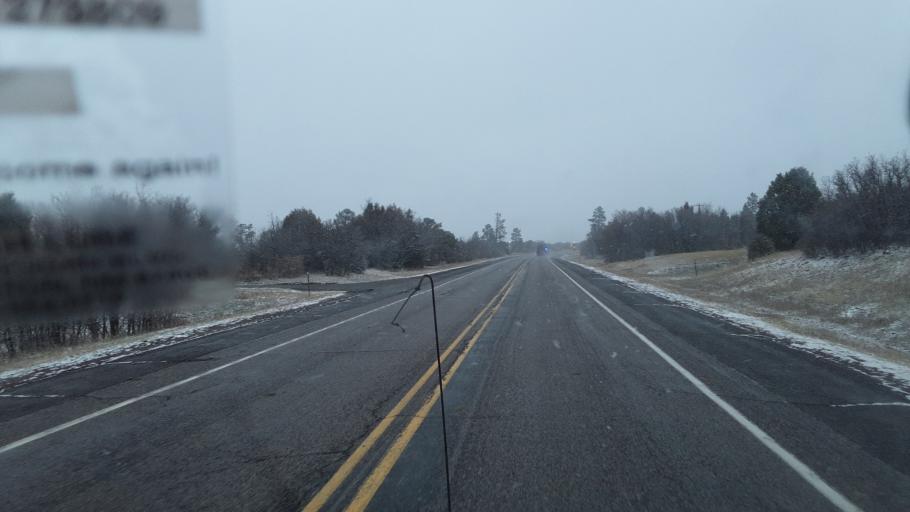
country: US
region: New Mexico
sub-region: Rio Arriba County
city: Tierra Amarilla
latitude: 36.8008
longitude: -106.5655
